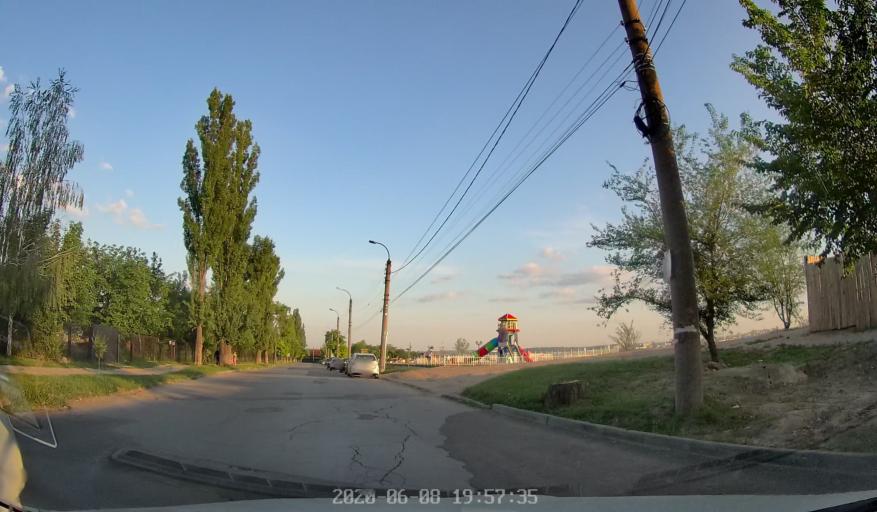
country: MD
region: Chisinau
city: Chisinau
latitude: 47.0151
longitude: 28.8824
